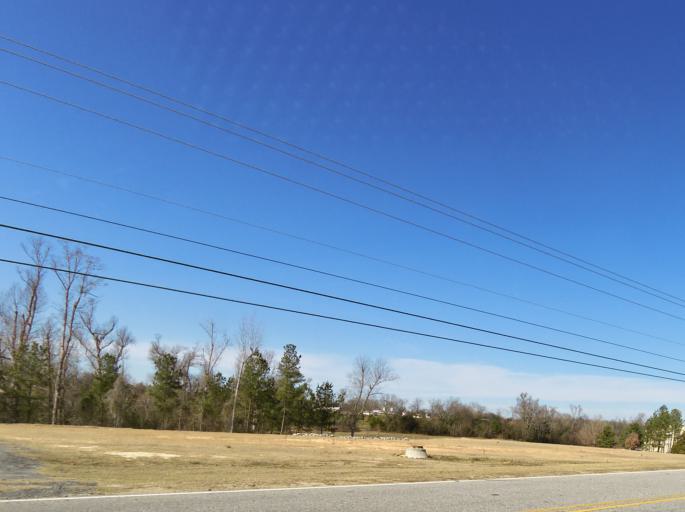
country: US
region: Georgia
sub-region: Bibb County
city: West Point
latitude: 32.8088
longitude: -83.7362
